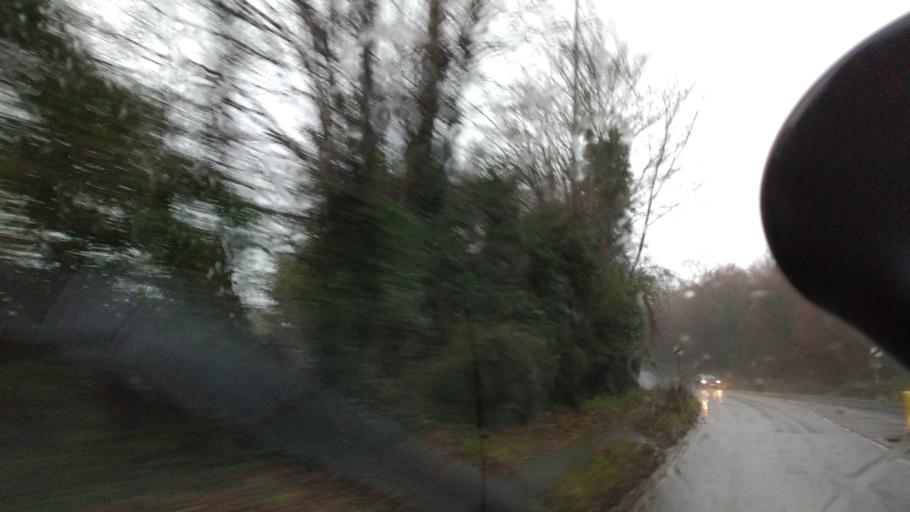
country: GB
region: England
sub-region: West Sussex
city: Arundel
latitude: 50.8542
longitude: -0.5666
